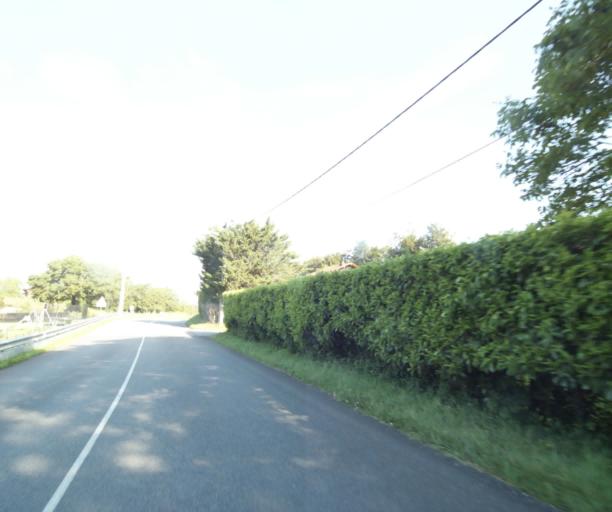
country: FR
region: Rhone-Alpes
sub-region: Departement de la Haute-Savoie
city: Armoy
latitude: 46.3455
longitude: 6.5273
